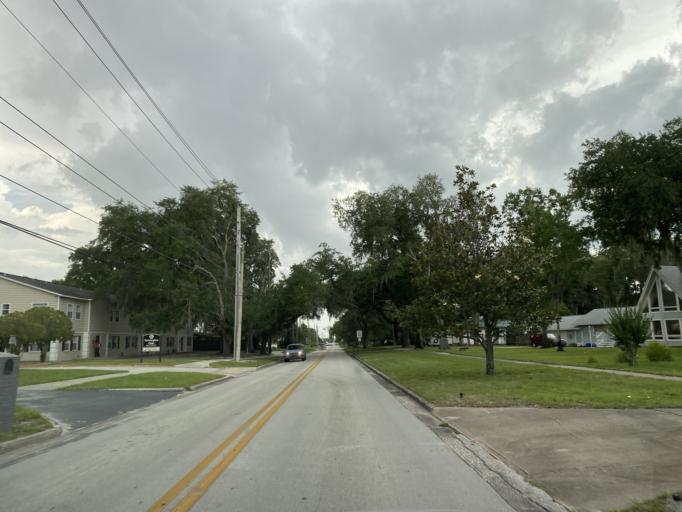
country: US
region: Florida
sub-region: Seminole County
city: Sanford
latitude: 28.8070
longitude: -81.2552
